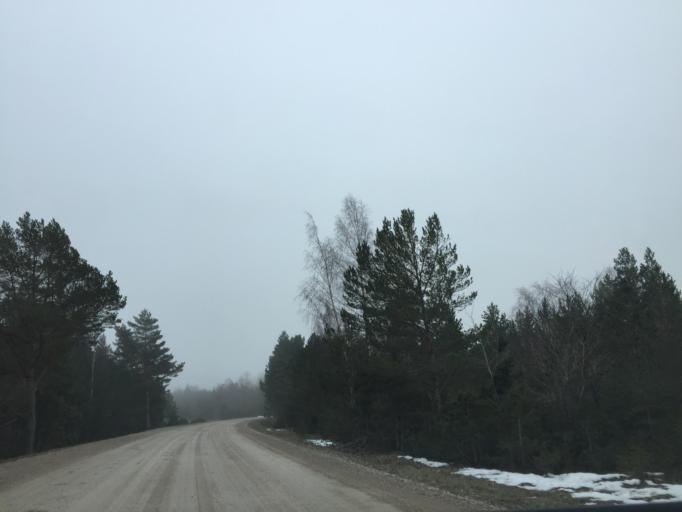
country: EE
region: Saare
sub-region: Kuressaare linn
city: Kuressaare
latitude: 58.4771
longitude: 22.0019
